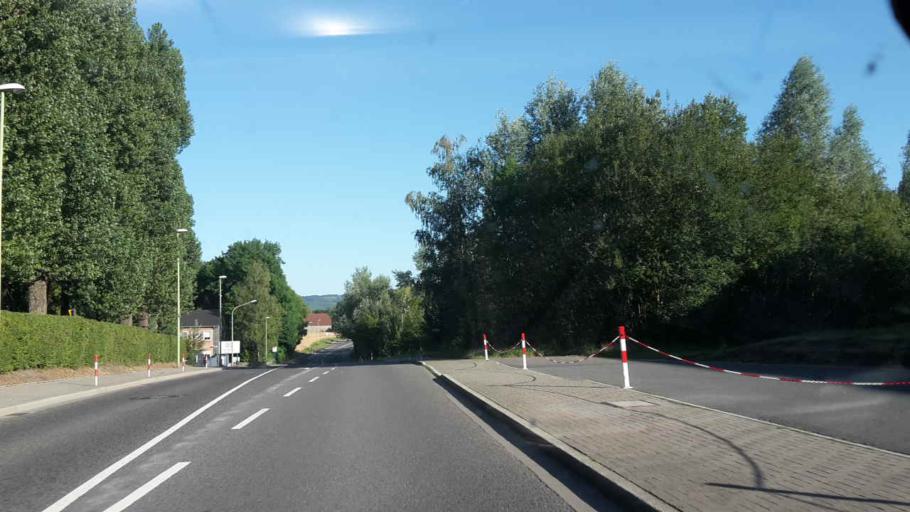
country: DE
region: North Rhine-Westphalia
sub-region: Regierungsbezirk Arnsberg
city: Hagen
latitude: 51.3752
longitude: 7.5285
